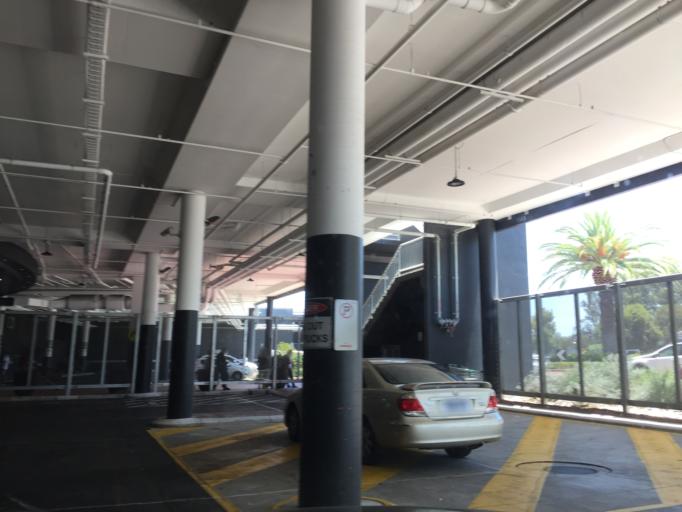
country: AU
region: Western Australia
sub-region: Canning
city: Cannington
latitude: -32.0198
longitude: 115.9391
